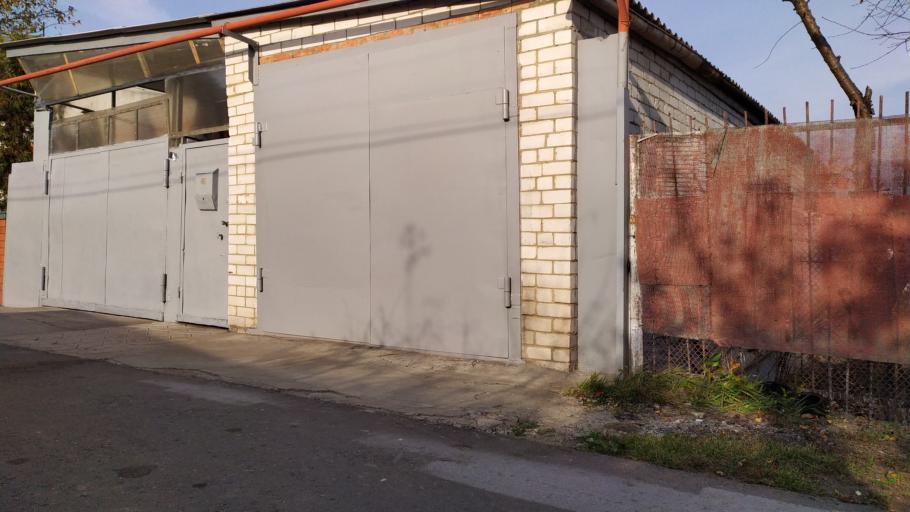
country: RU
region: Kursk
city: Kursk
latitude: 51.6438
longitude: 36.1475
